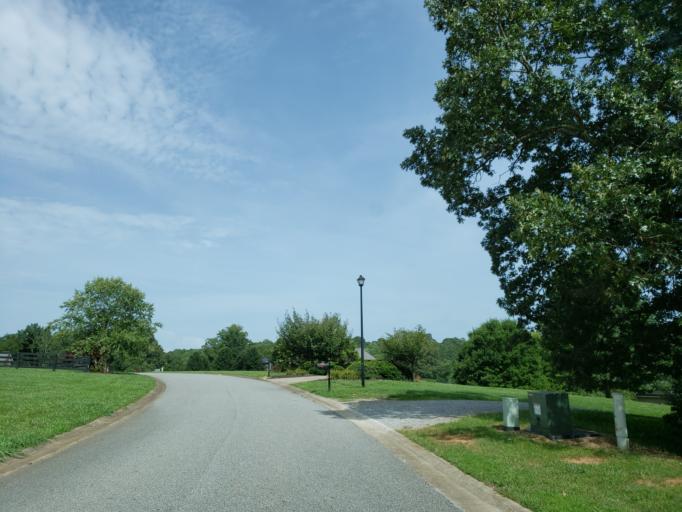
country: US
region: Georgia
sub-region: Cherokee County
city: Ball Ground
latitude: 34.3097
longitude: -84.4442
